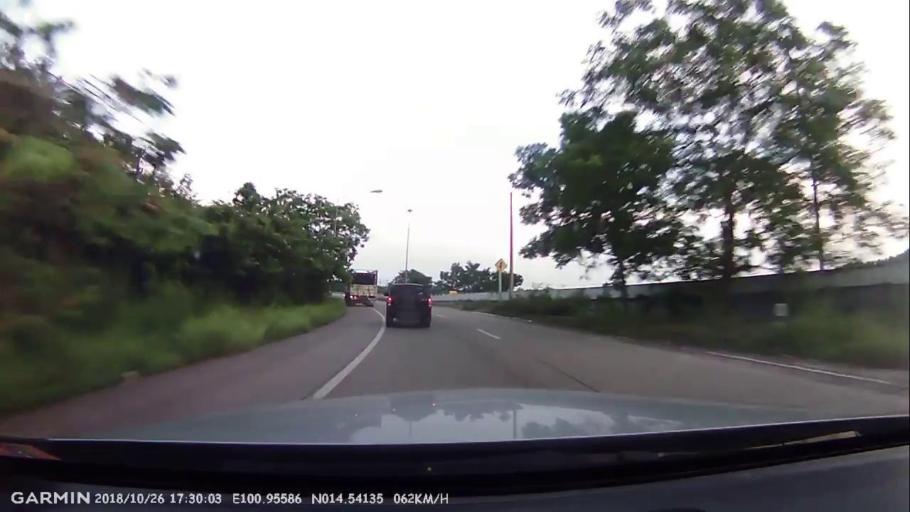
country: TH
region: Sara Buri
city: Saraburi
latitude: 14.5412
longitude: 100.9560
